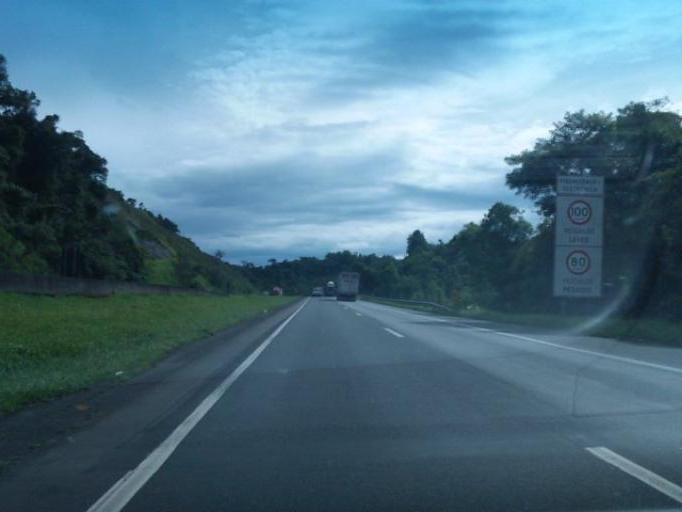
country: BR
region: Sao Paulo
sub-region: Cajati
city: Cajati
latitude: -24.9689
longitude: -48.3473
